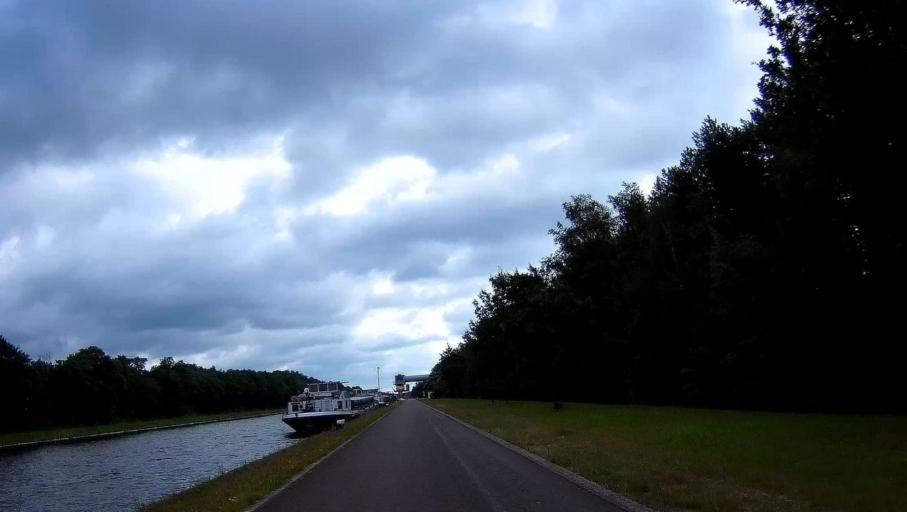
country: BE
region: Flanders
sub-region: Provincie Limburg
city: Lommel
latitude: 51.2414
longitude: 5.2364
